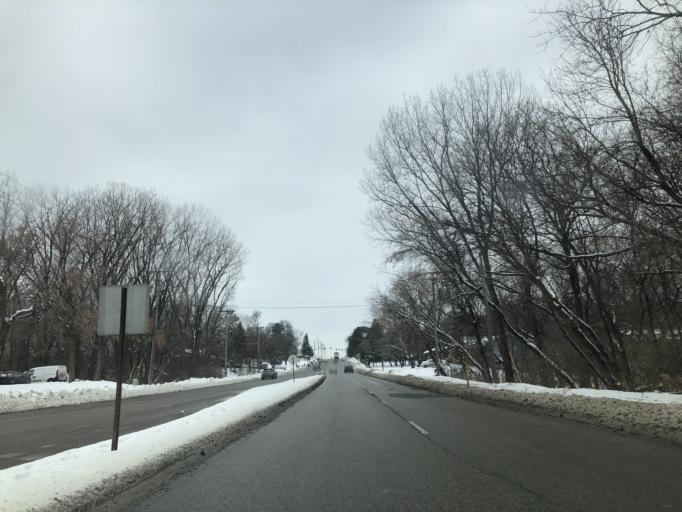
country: US
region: Minnesota
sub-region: Hennepin County
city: Osseo
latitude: 45.0946
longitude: -93.3872
